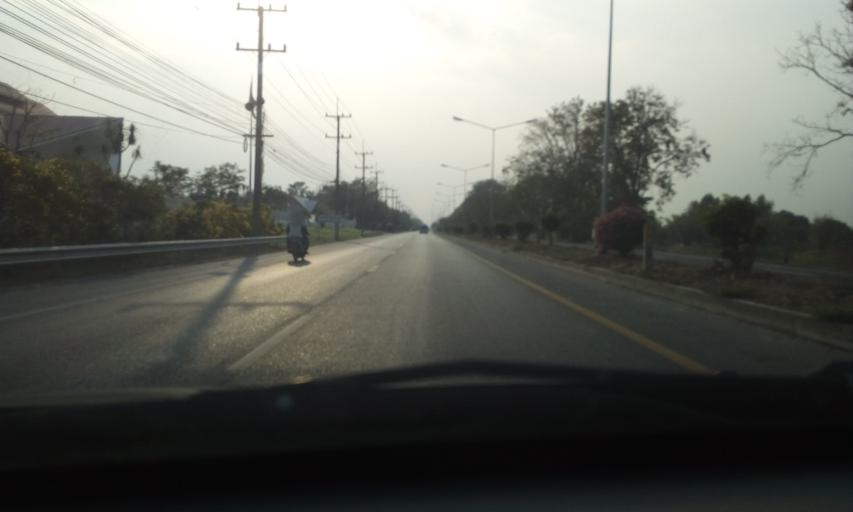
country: TH
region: Nakhon Nayok
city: Ban Na
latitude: 14.2128
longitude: 101.1000
